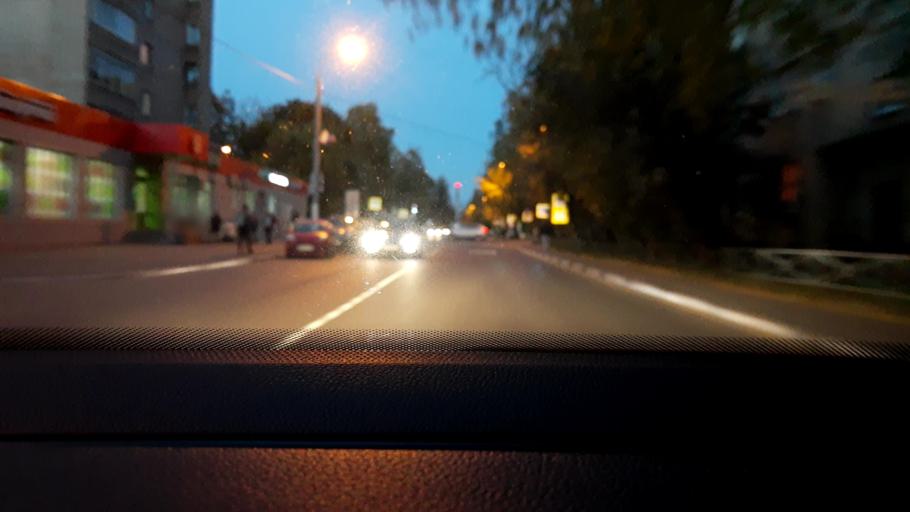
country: RU
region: Moskovskaya
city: Dolgoprudnyy
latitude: 55.9414
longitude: 37.5123
